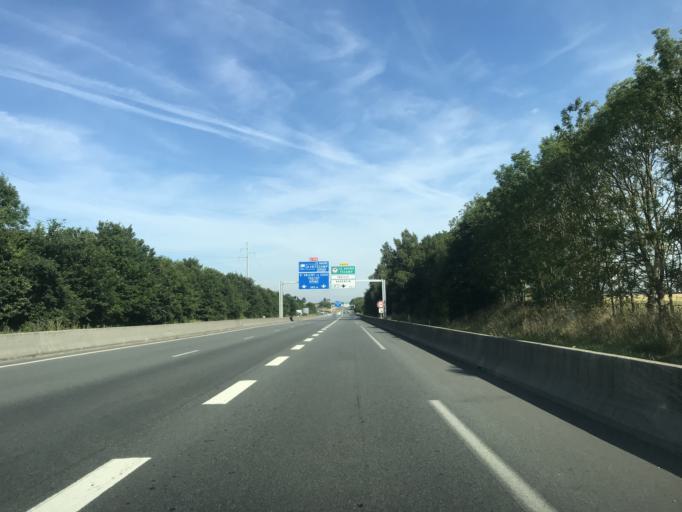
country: FR
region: Haute-Normandie
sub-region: Departement de la Seine-Maritime
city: Roumare
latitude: 49.5186
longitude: 0.9766
